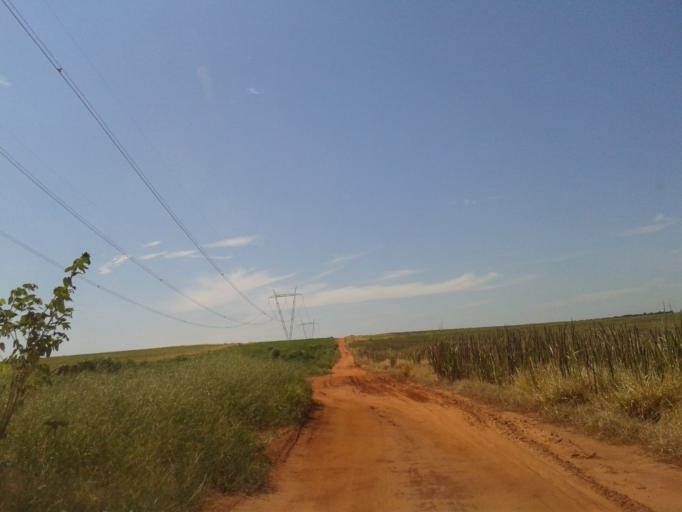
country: BR
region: Minas Gerais
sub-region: Santa Vitoria
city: Santa Vitoria
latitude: -19.0806
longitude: -50.4569
